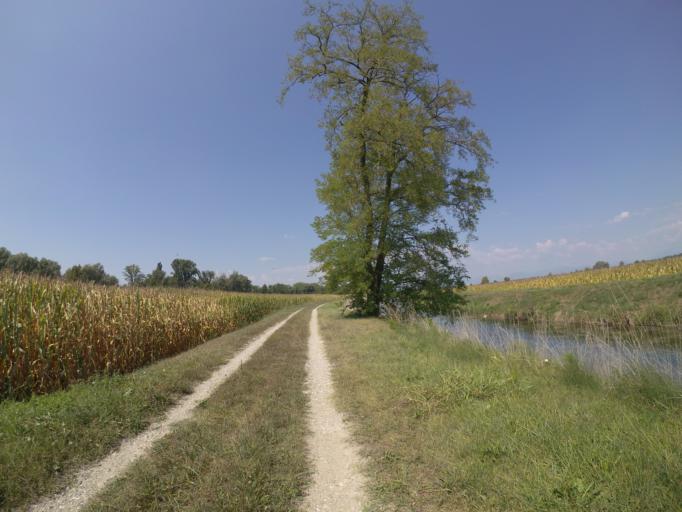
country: IT
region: Friuli Venezia Giulia
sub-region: Provincia di Udine
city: Codroipo
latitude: 45.9339
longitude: 13.0015
